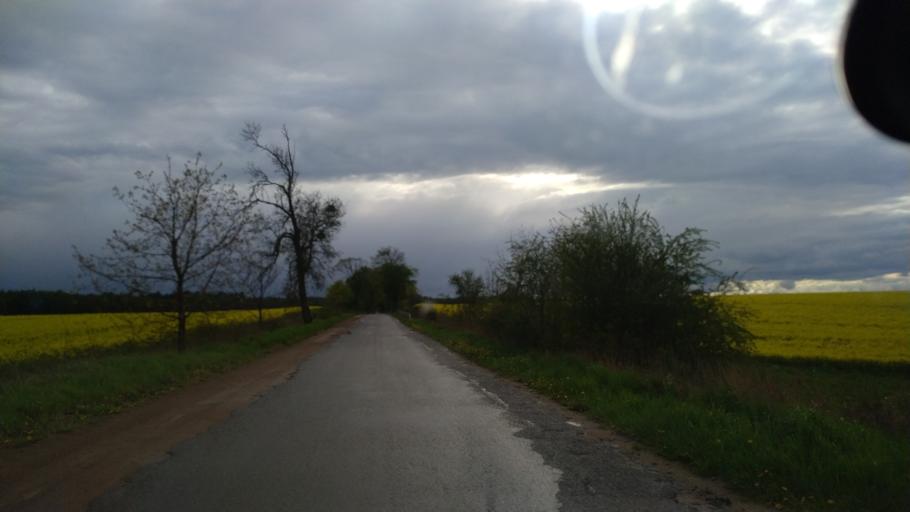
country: PL
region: Pomeranian Voivodeship
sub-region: Powiat starogardzki
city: Smetowo Graniczne
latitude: 53.7154
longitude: 18.6033
